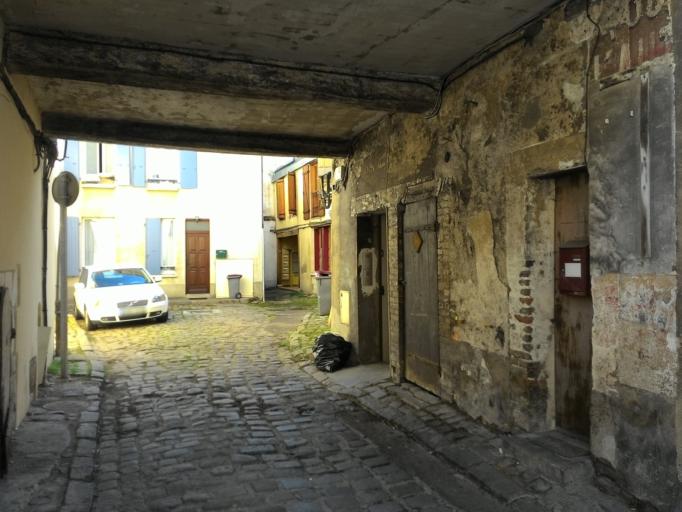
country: FR
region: Bourgogne
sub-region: Departement de l'Yonne
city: Sens
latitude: 48.1961
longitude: 3.2831
